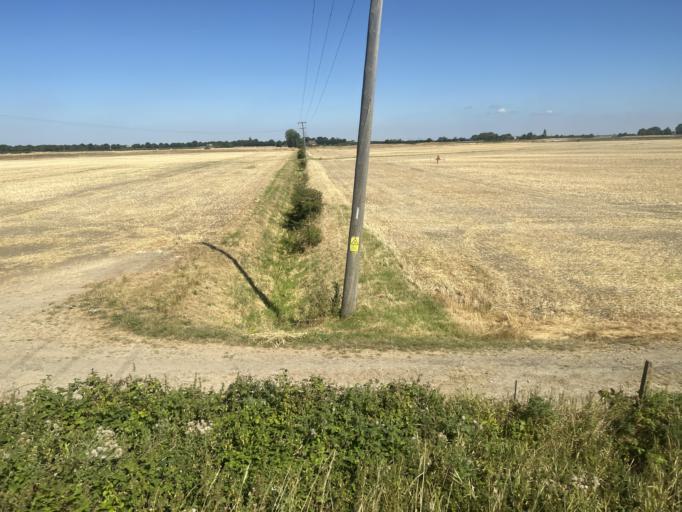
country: GB
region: England
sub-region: Lincolnshire
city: Donington
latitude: 52.9677
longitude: -0.2036
